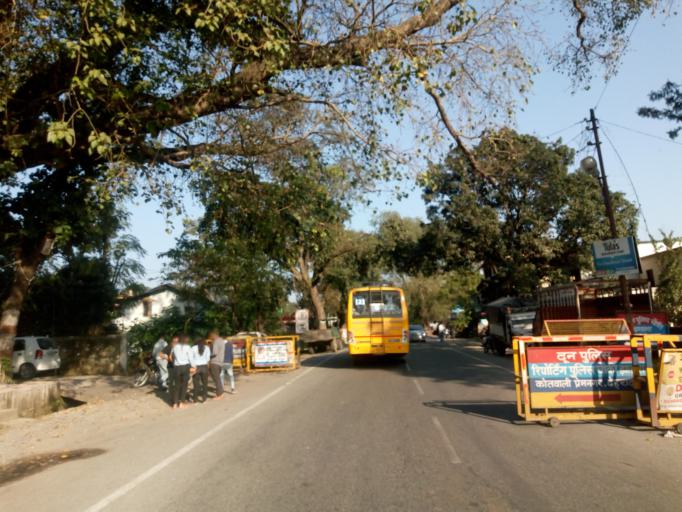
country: IN
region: Uttarakhand
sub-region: Dehradun
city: Dehradun
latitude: 30.3443
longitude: 77.9158
